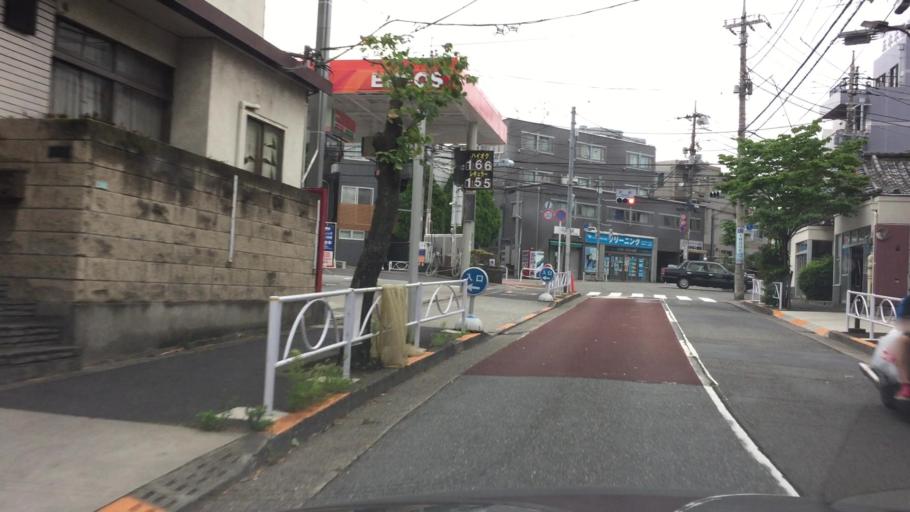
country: JP
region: Tokyo
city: Tokyo
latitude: 35.6409
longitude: 139.6865
